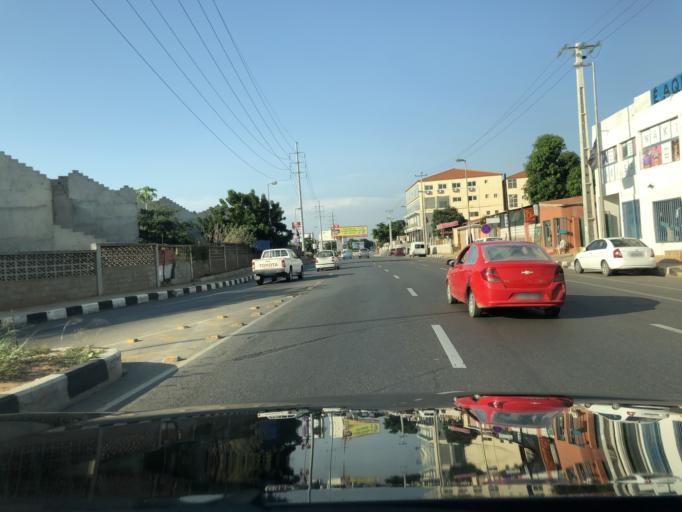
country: AO
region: Luanda
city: Luanda
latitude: -8.8962
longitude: 13.1800
